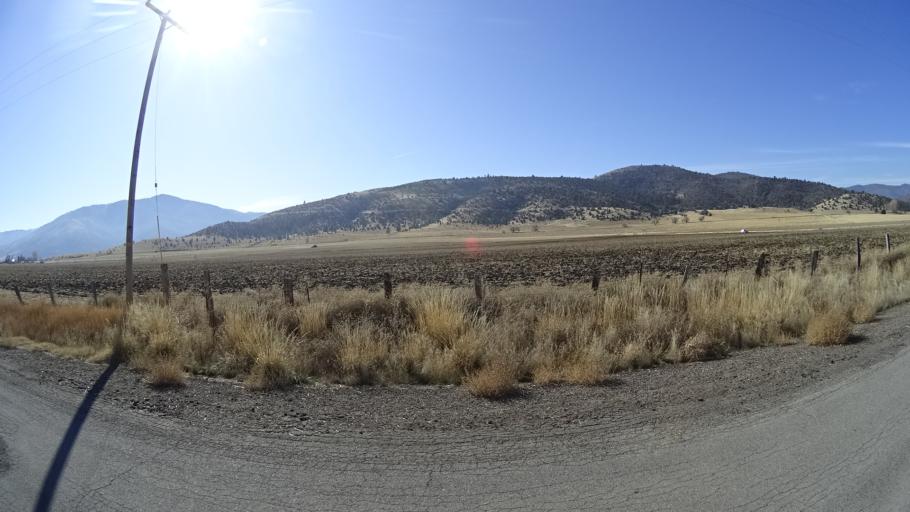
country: US
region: California
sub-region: Siskiyou County
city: Weed
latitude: 41.5243
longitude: -122.5291
